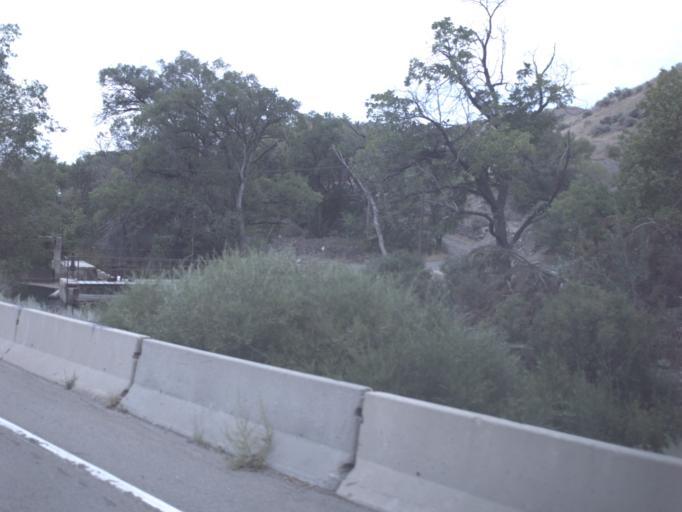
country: US
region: Utah
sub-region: Utah County
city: Cedar Hills
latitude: 40.4324
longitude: -111.7514
